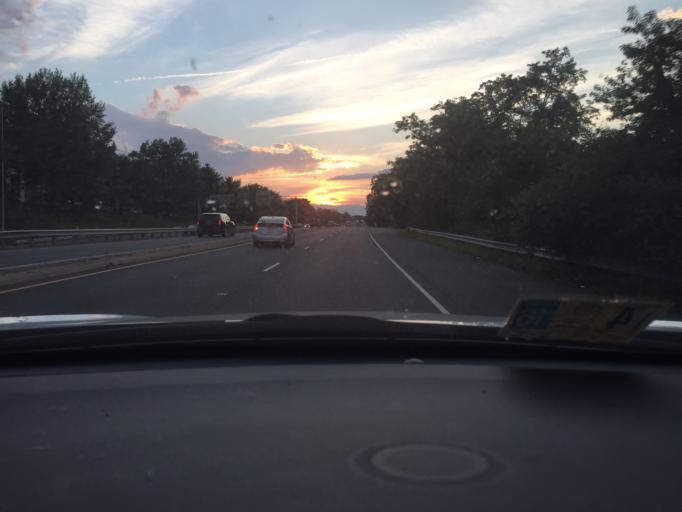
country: US
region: Virginia
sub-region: City of Fairfax
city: Fairfax
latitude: 38.8638
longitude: -77.3520
